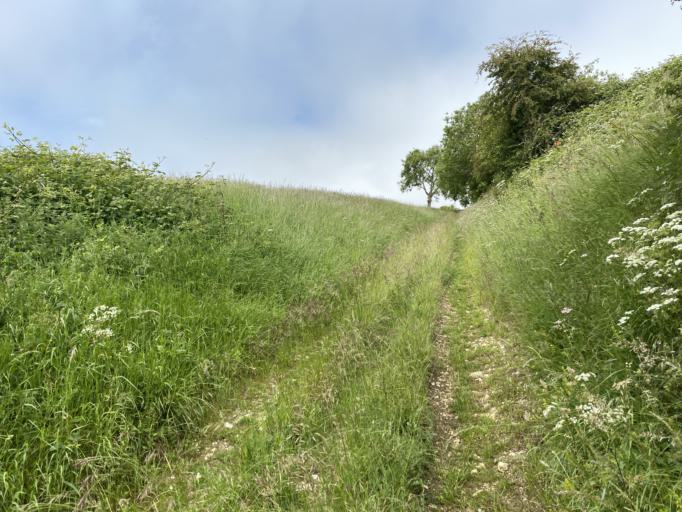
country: GB
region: England
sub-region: East Riding of Yorkshire
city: Wold Newton
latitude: 54.0968
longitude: -0.4748
